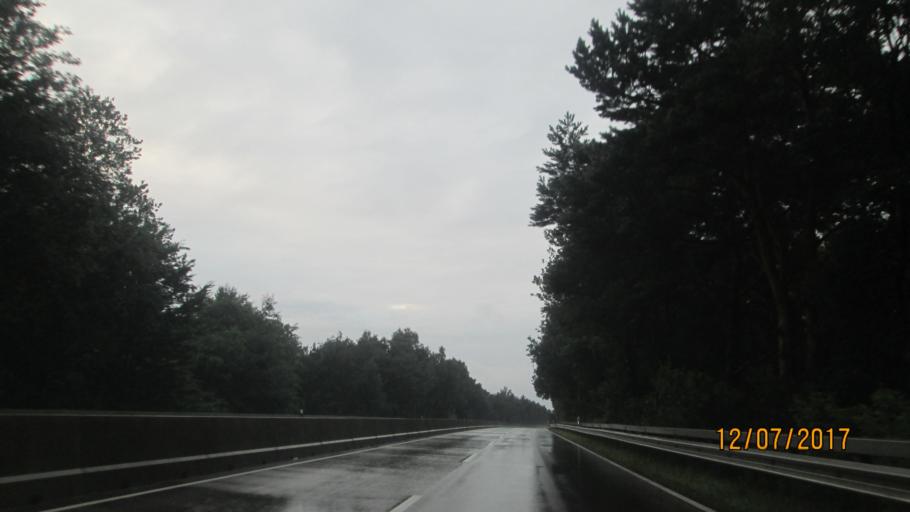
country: DE
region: Lower Saxony
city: Ribbesbuttel
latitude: 52.4496
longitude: 10.5350
